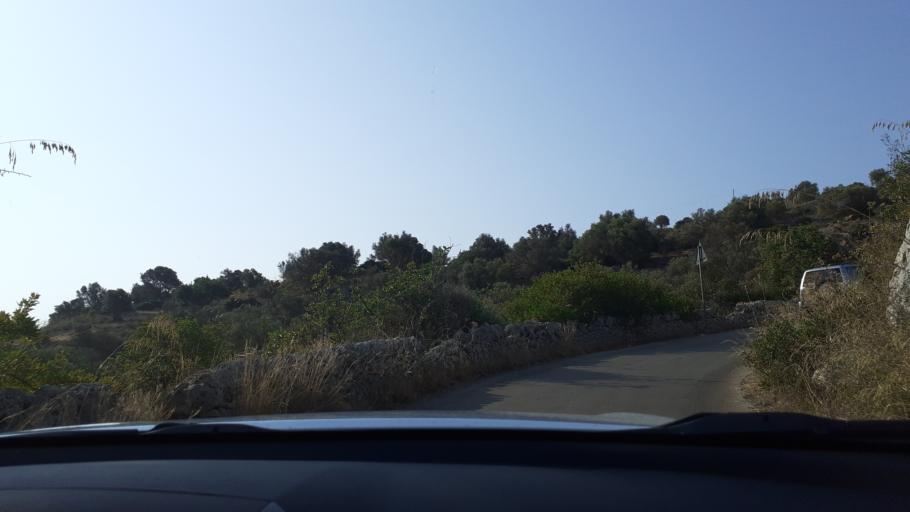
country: IT
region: Sicily
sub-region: Provincia di Siracusa
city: Cassibile
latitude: 36.9776
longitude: 15.1604
